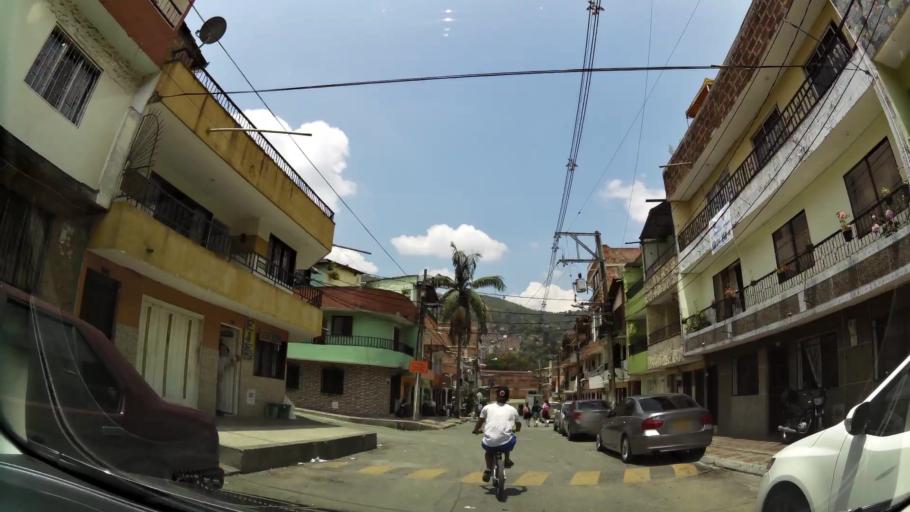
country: CO
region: Antioquia
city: Itagui
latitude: 6.1726
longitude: -75.6142
